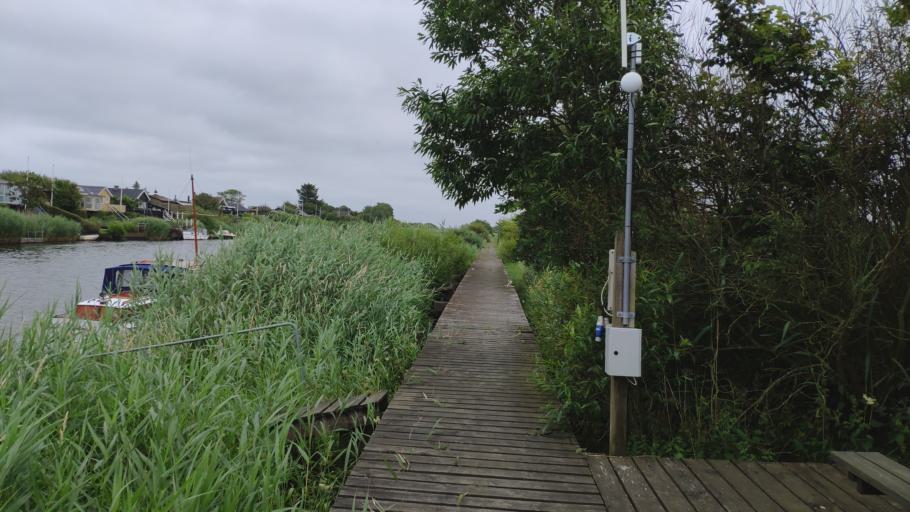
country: DK
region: South Denmark
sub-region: Esbjerg Kommune
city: Ribe
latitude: 55.3383
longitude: 8.6817
